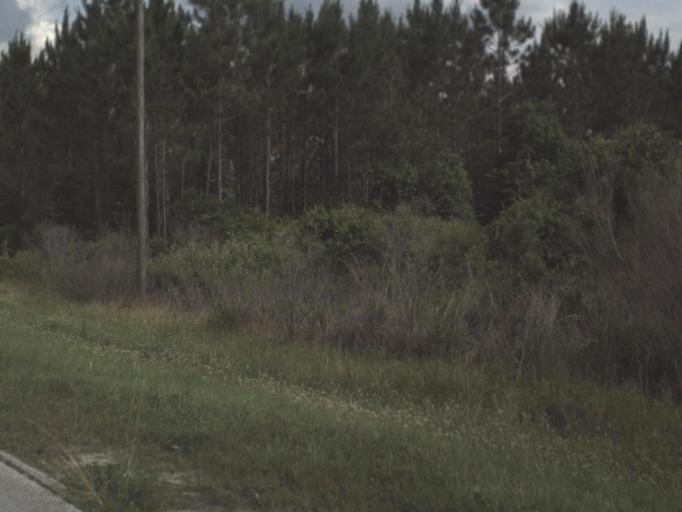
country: US
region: Florida
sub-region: Baker County
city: Macclenny
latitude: 30.5141
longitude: -82.2713
